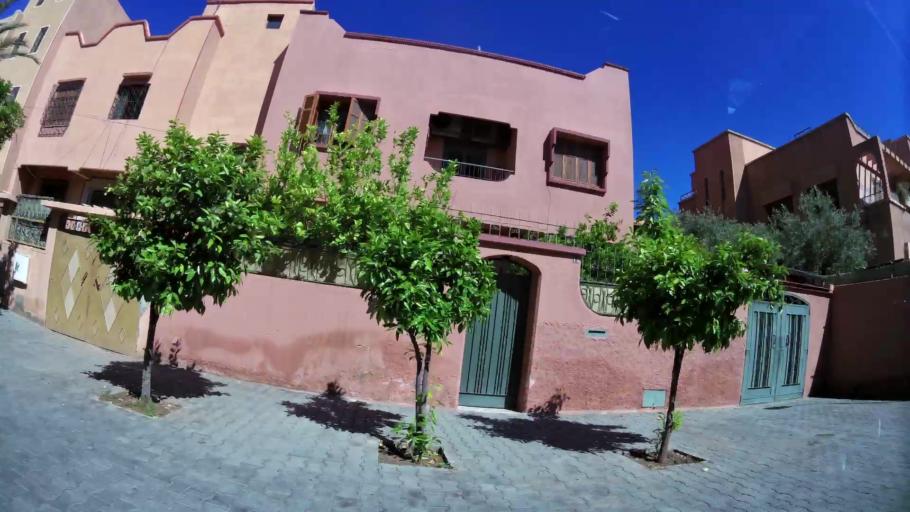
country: MA
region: Marrakech-Tensift-Al Haouz
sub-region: Marrakech
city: Marrakesh
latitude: 31.6439
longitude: -8.0113
